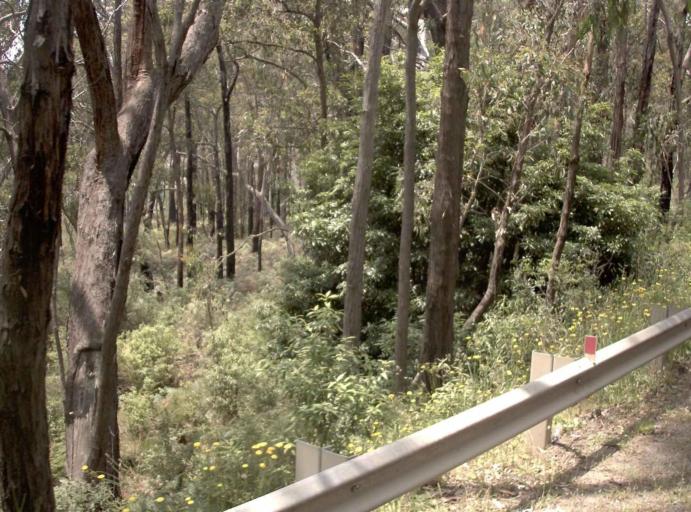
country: AU
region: Victoria
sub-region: Latrobe
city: Traralgon
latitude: -38.3153
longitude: 146.7196
